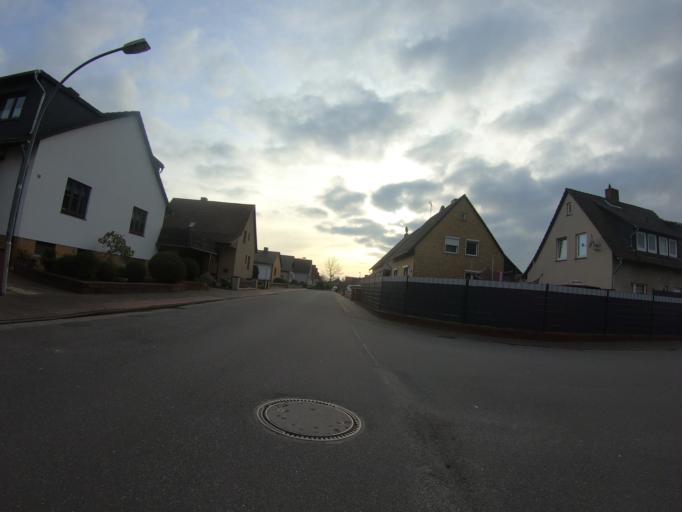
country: DE
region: Lower Saxony
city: Sassenburg
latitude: 52.5107
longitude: 10.5917
